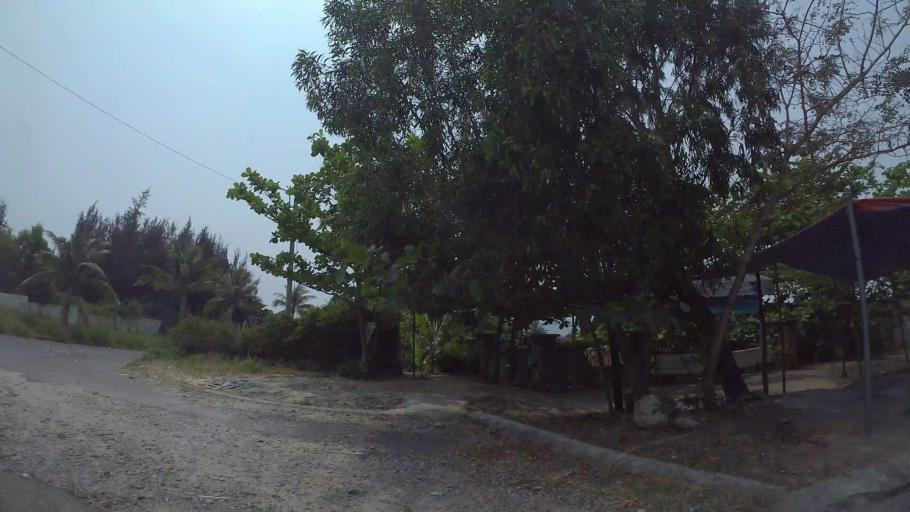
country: VN
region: Da Nang
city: Son Tra
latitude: 16.0973
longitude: 108.2677
